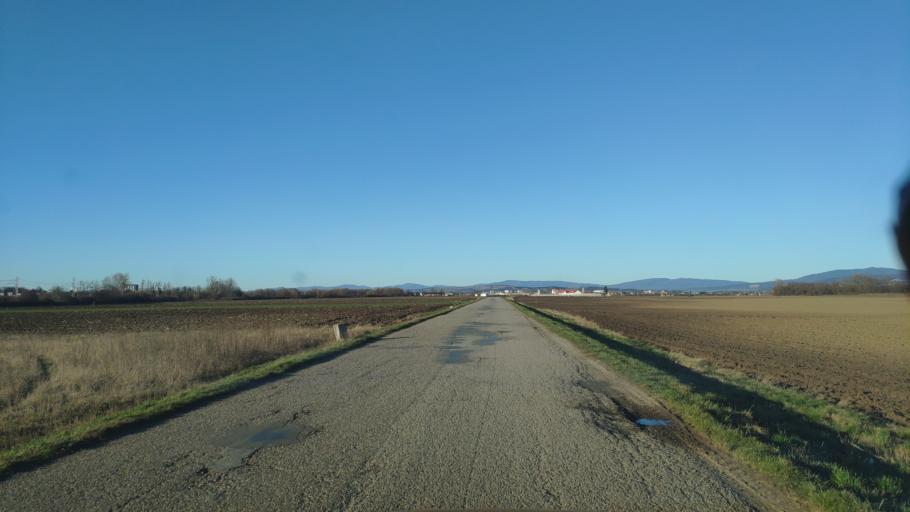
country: HU
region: Borsod-Abauj-Zemplen
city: Gonc
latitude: 48.5908
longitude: 21.3122
